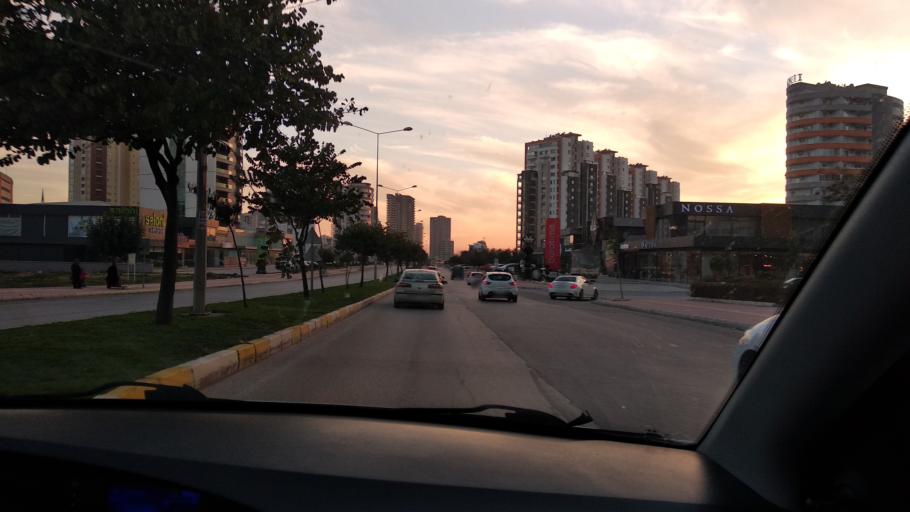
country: TR
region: Mersin
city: Mercin
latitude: 36.8069
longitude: 34.5879
